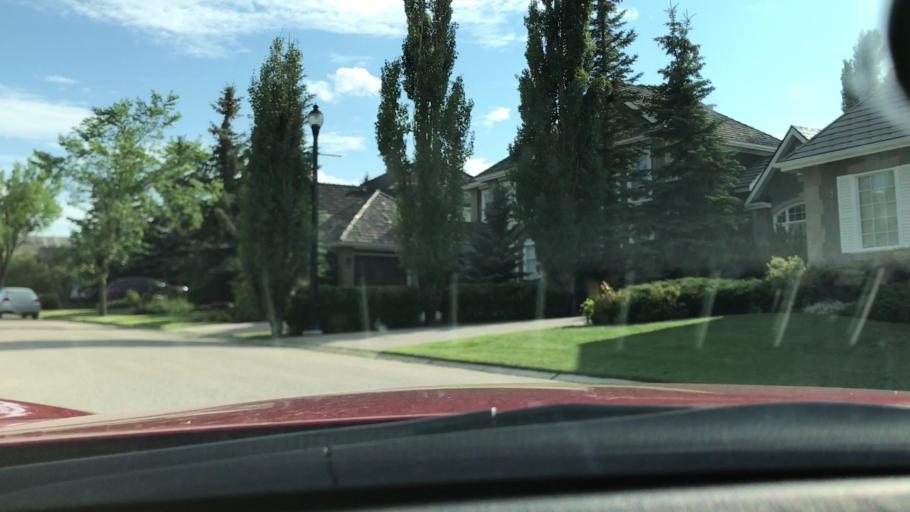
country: CA
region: Alberta
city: Calgary
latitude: 51.0264
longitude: -114.1759
